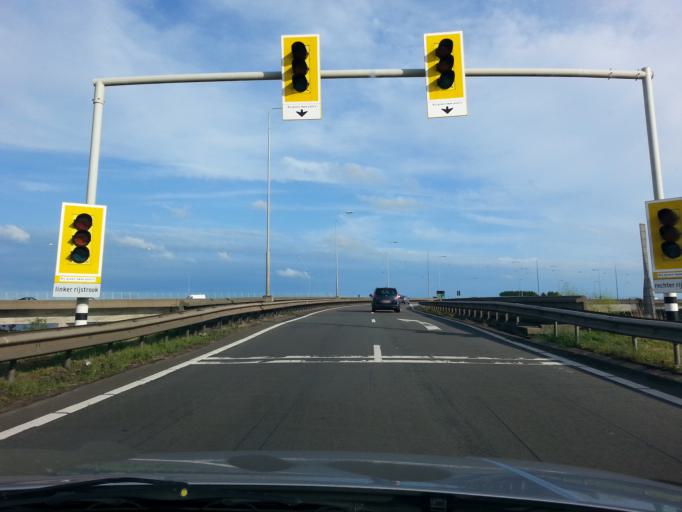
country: NL
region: North Holland
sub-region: Gemeente Diemen
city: Diemen
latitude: 52.3659
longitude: 4.9697
